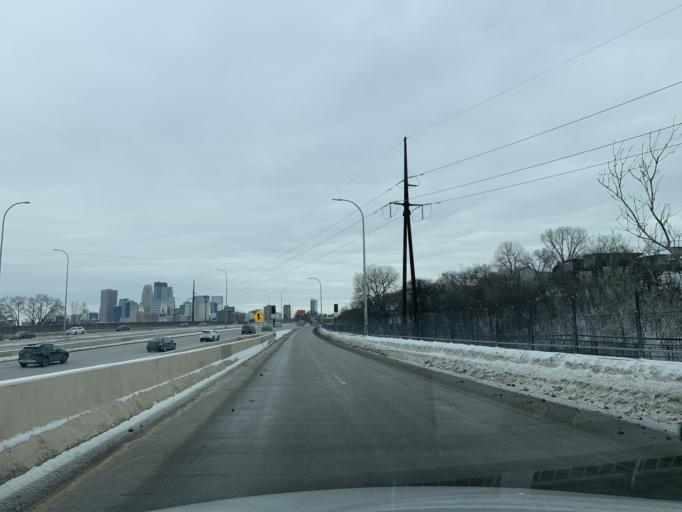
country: US
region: Minnesota
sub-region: Hennepin County
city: Minneapolis
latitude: 44.9693
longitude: -93.3073
